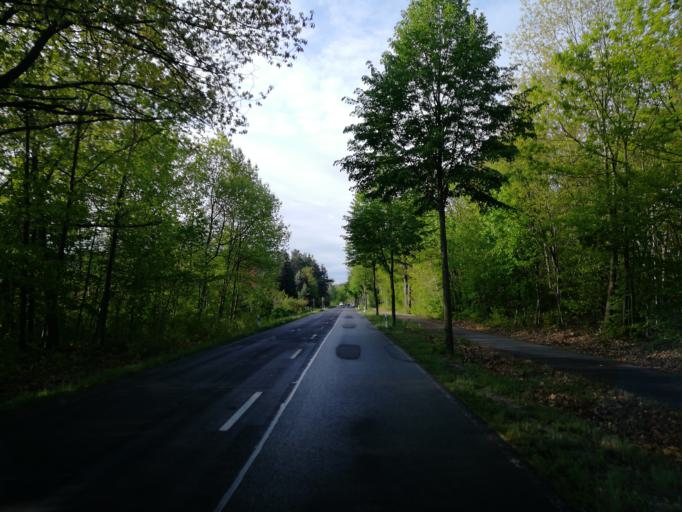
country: DE
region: Brandenburg
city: Lauchhammer
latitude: 51.5113
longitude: 13.7485
